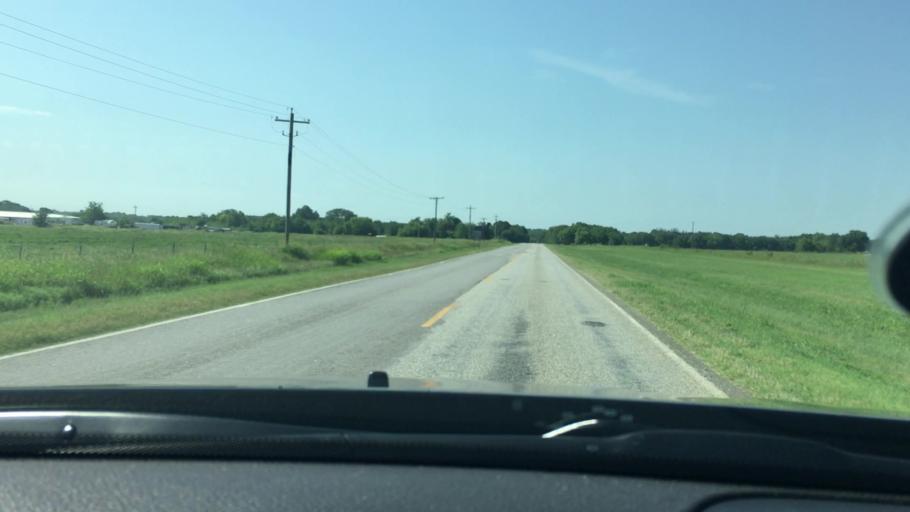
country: US
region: Oklahoma
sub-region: Johnston County
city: Tishomingo
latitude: 34.3420
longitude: -96.4219
